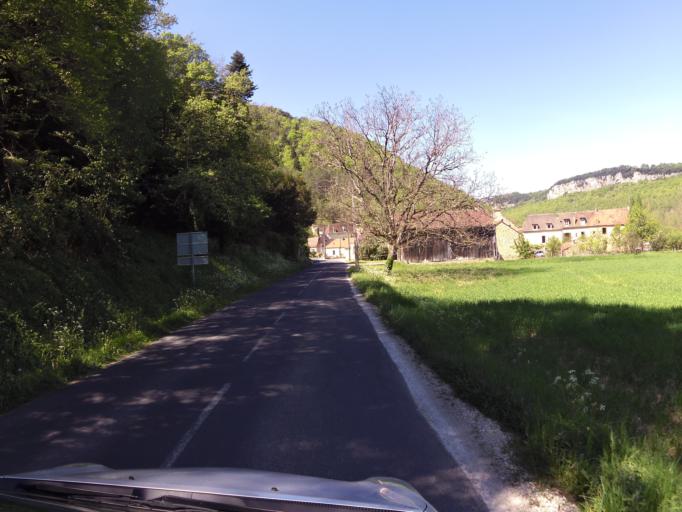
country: FR
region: Aquitaine
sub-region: Departement de la Dordogne
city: Cenac-et-Saint-Julien
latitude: 44.7949
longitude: 1.1610
